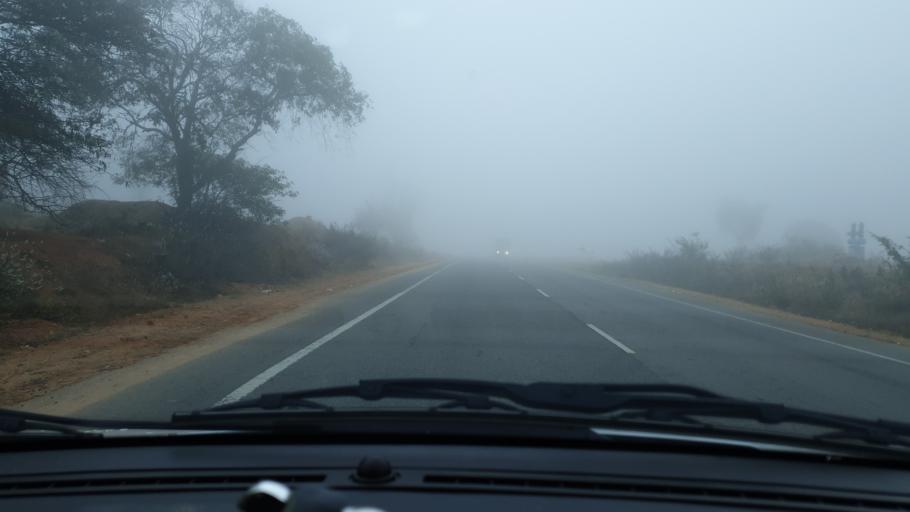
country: IN
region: Telangana
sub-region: Mahbubnagar
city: Nagar Karnul
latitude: 16.6839
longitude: 78.5247
